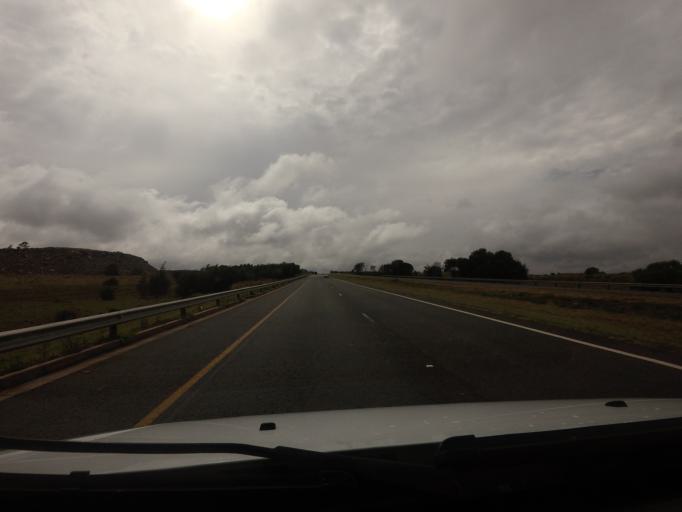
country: ZA
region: Mpumalanga
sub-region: Nkangala District Municipality
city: Witbank
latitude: -25.8695
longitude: 29.0499
